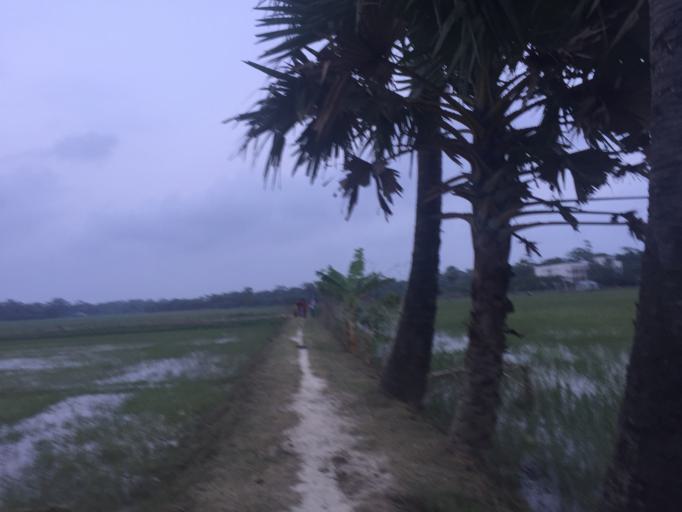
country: BD
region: Barisal
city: Mathba
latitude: 22.1920
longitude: 89.9347
